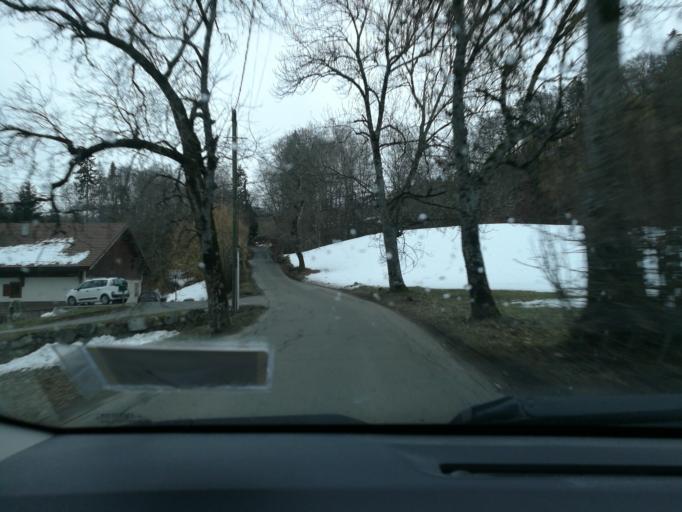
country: FR
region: Rhone-Alpes
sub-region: Departement de la Haute-Savoie
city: Domancy
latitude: 45.9167
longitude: 6.6300
